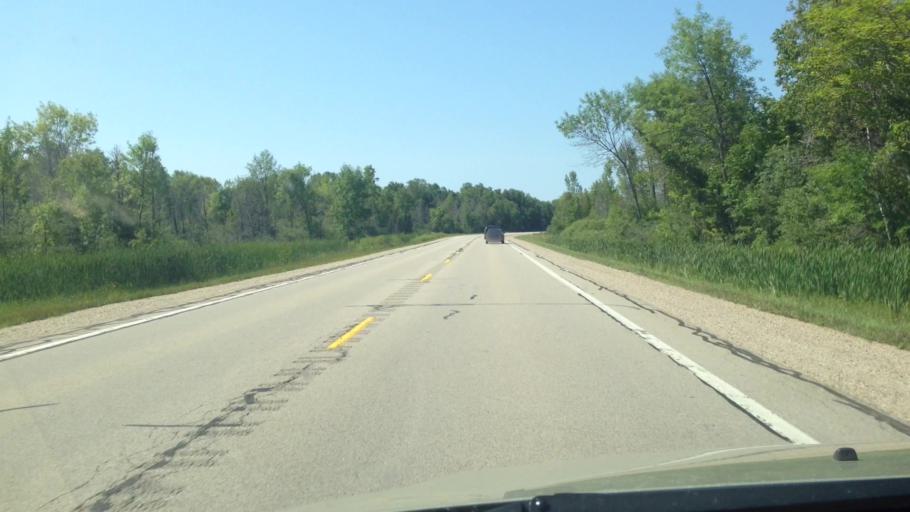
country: US
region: Michigan
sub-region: Menominee County
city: Menominee
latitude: 45.3833
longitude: -87.3750
